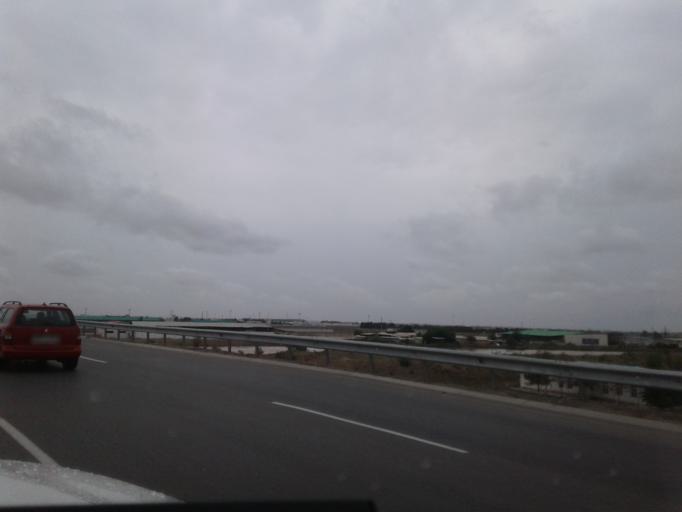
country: TM
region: Mary
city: Mary
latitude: 37.6074
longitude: 61.9191
